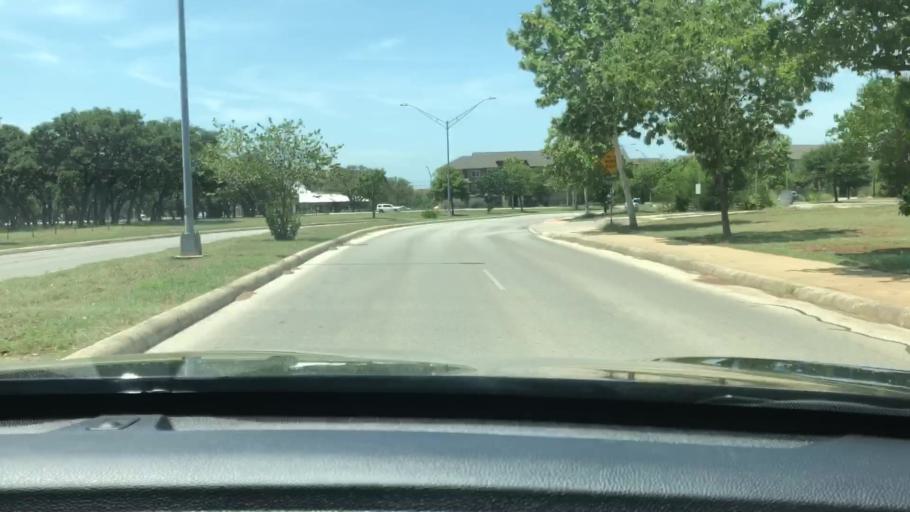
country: US
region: Texas
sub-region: Bexar County
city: Helotes
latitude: 29.5616
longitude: -98.6538
